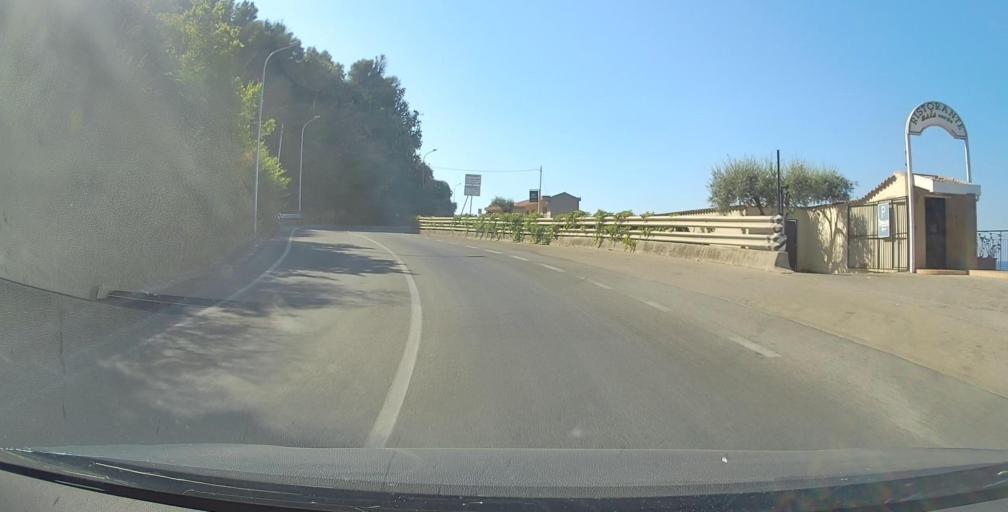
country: IT
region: Sicily
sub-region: Messina
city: Naso
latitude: 38.1524
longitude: 14.7824
